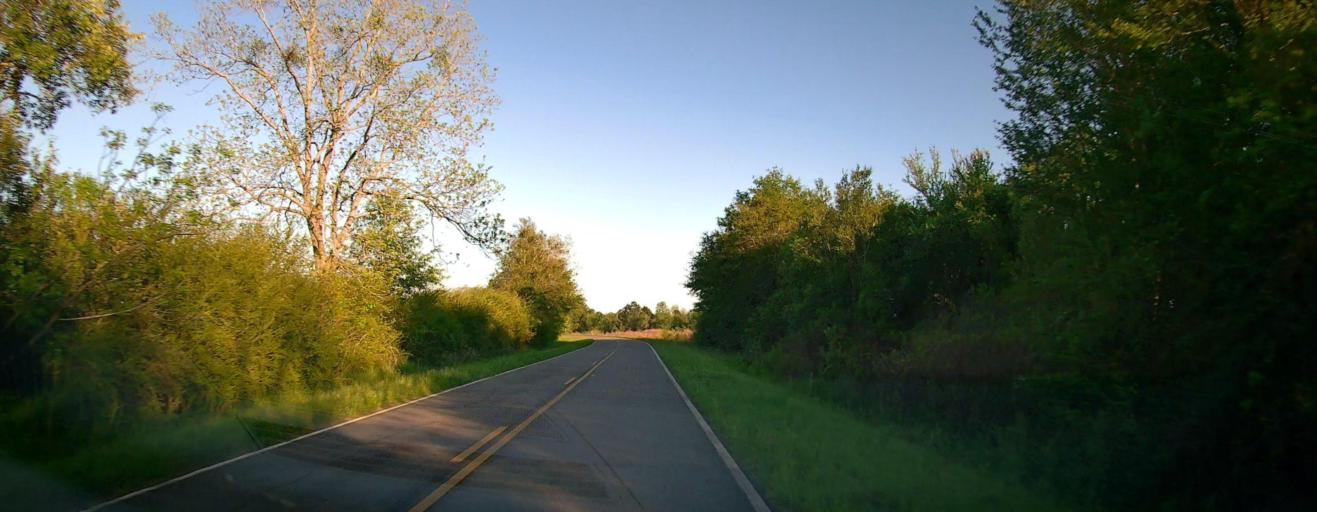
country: US
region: Georgia
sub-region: Ben Hill County
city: Fitzgerald
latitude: 31.6816
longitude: -83.2243
